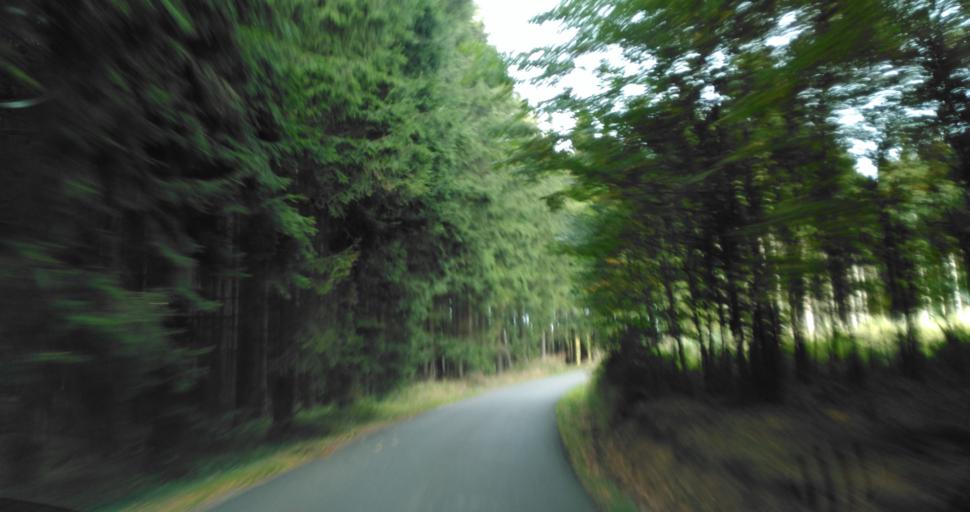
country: CZ
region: Plzensky
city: Zbiroh
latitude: 49.9266
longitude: 13.7971
